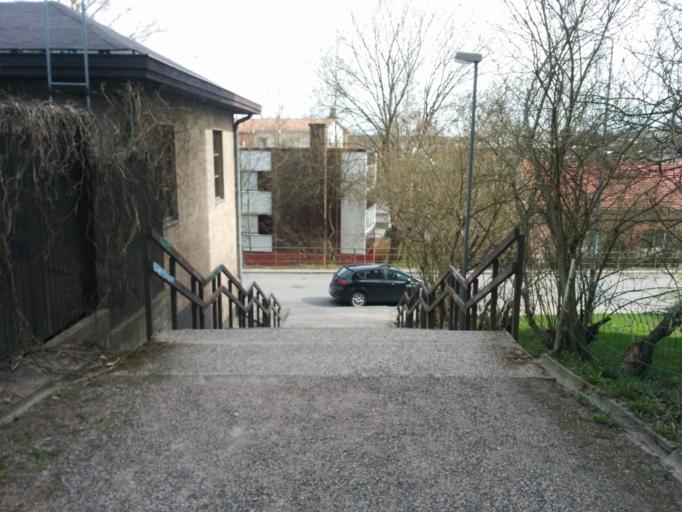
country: FI
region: Haeme
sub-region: Riihimaeki
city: Riihimaeki
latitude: 60.7412
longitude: 24.7709
